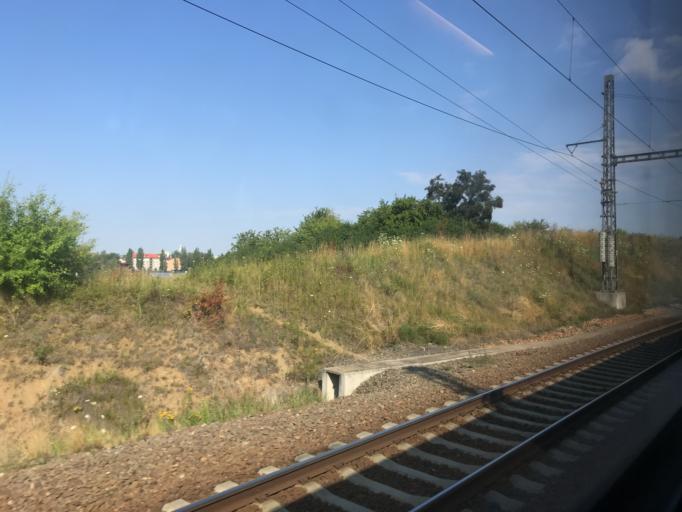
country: CZ
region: Jihocesky
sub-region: Okres Tabor
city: Tabor
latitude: 49.4195
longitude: 14.6711
